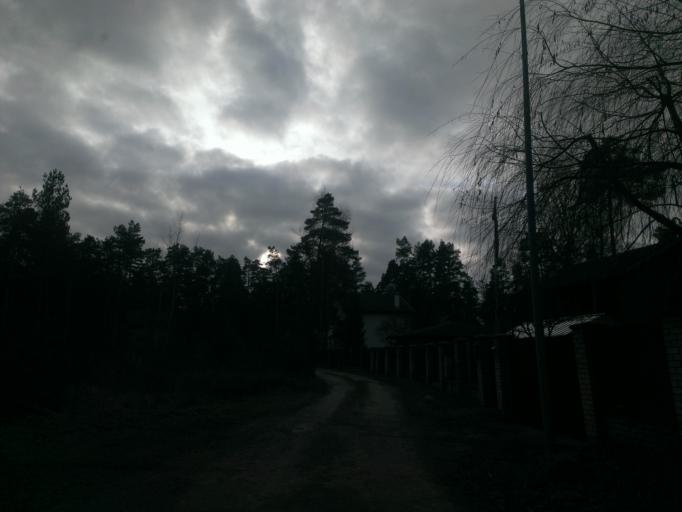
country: LV
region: Riga
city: Bergi
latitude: 57.0062
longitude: 24.3341
